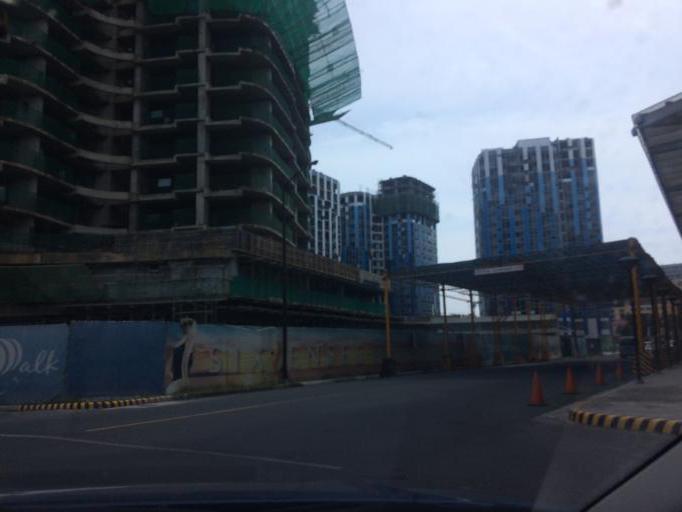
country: PH
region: Metro Manila
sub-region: Makati City
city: Makati City
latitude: 14.5409
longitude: 120.9904
